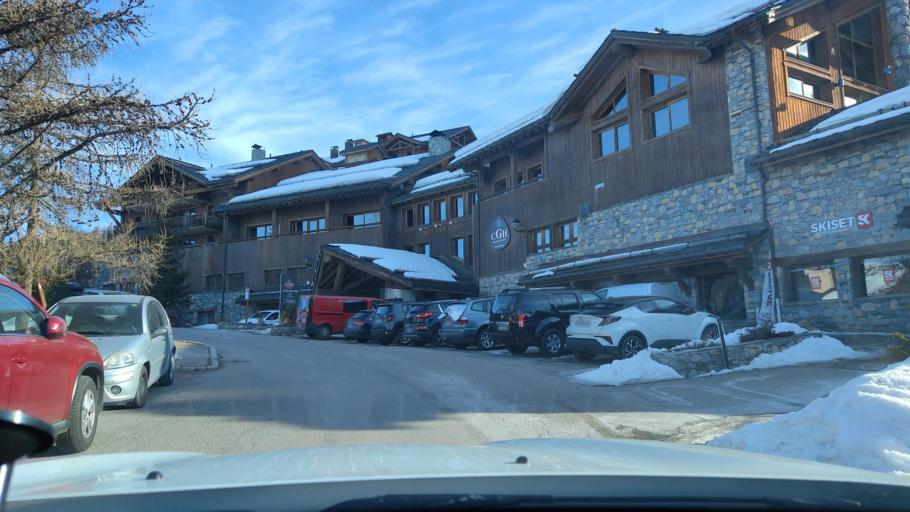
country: FR
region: Rhone-Alpes
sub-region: Departement de la Savoie
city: Bourg-Saint-Maurice
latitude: 45.5546
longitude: 6.7635
